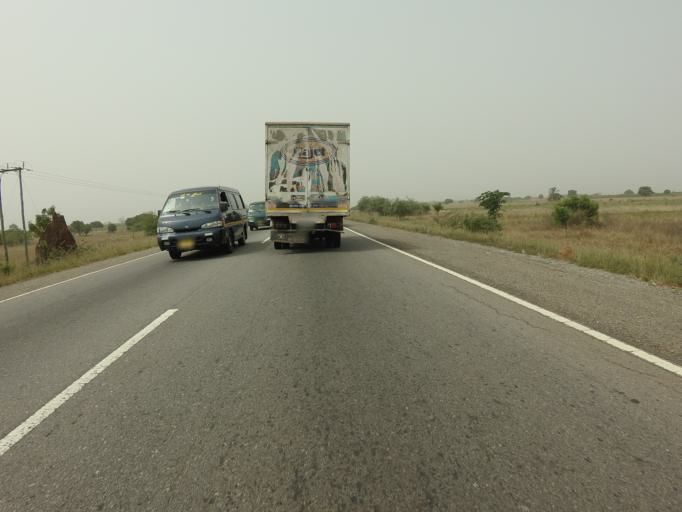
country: GH
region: Volta
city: Anloga
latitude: 5.8879
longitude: 0.4579
